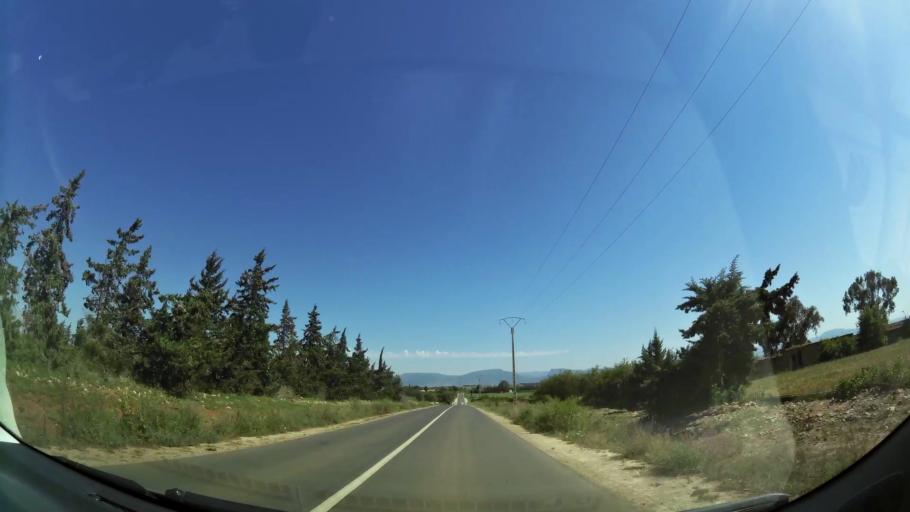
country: MA
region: Oriental
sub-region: Berkane-Taourirt
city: Madagh
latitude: 35.0254
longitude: -2.4107
